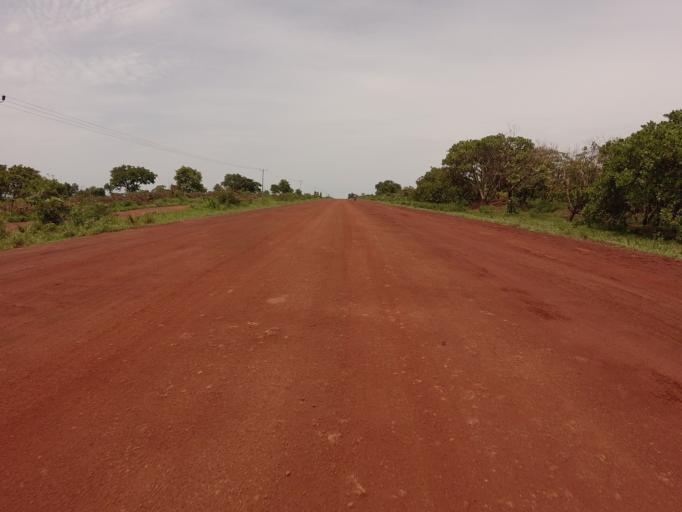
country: GH
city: Kpandae
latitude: 8.8326
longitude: 0.0599
